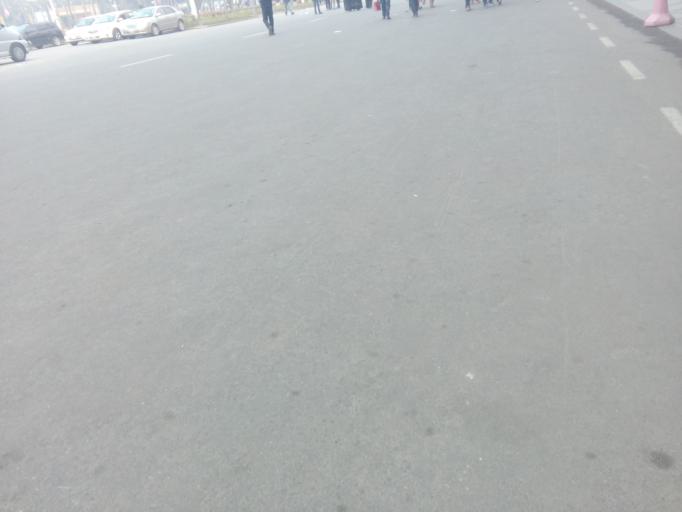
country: BD
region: Dhaka
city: Azimpur
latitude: 23.7697
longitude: 90.3813
